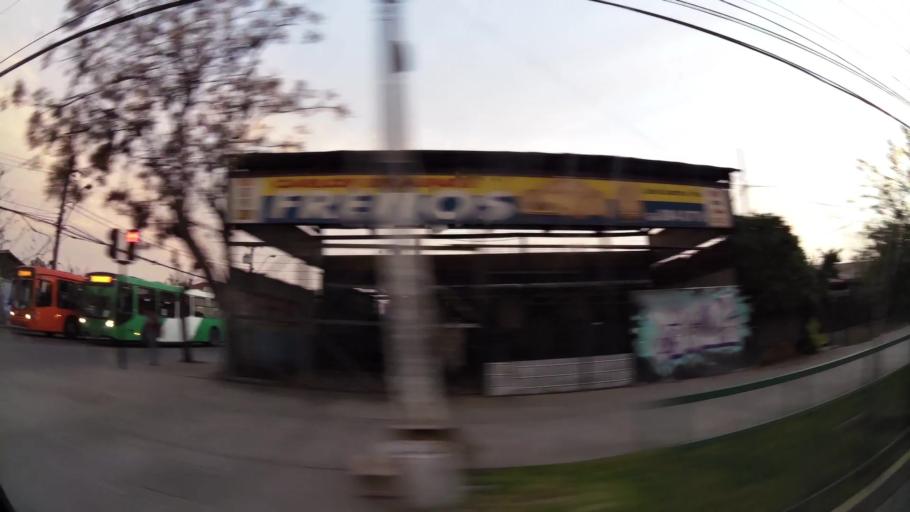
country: CL
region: Santiago Metropolitan
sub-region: Provincia de Santiago
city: Lo Prado
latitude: -33.5111
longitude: -70.7473
